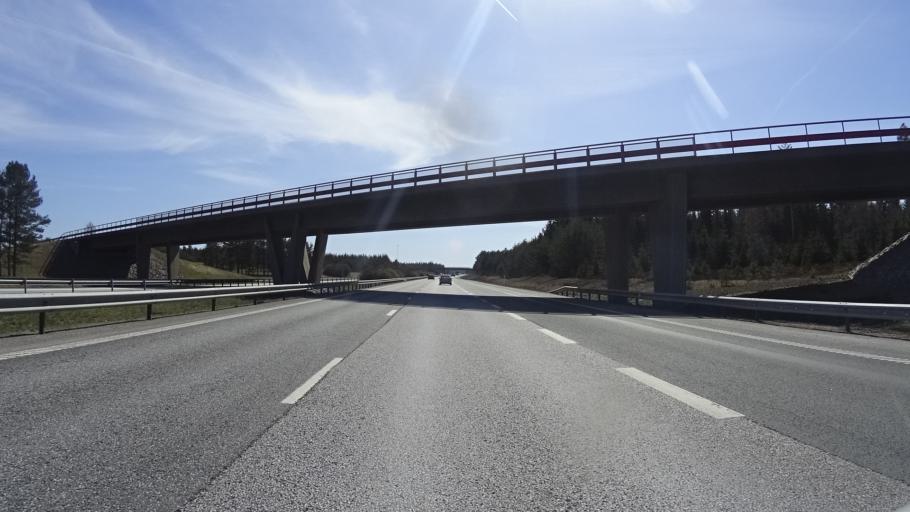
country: SE
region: Joenkoeping
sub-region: Jonkopings Kommun
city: Odensjo
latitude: 57.6270
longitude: 14.1843
